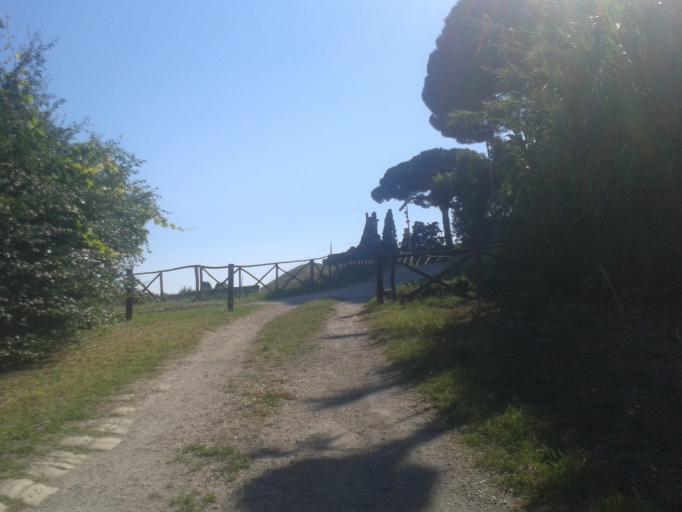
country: IT
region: Campania
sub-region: Provincia di Napoli
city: Pompei
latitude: 40.7537
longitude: 14.4849
